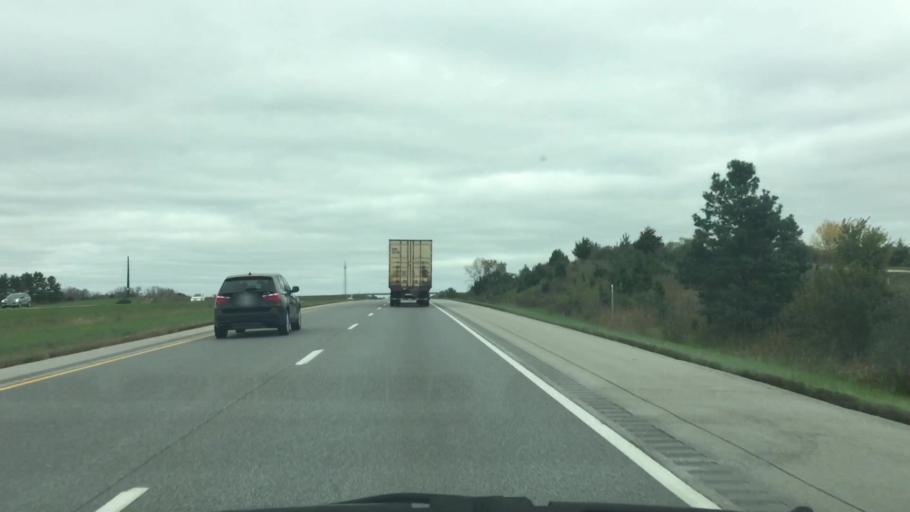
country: US
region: Iowa
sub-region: Warren County
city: Norwalk
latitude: 41.4723
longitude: -93.7788
